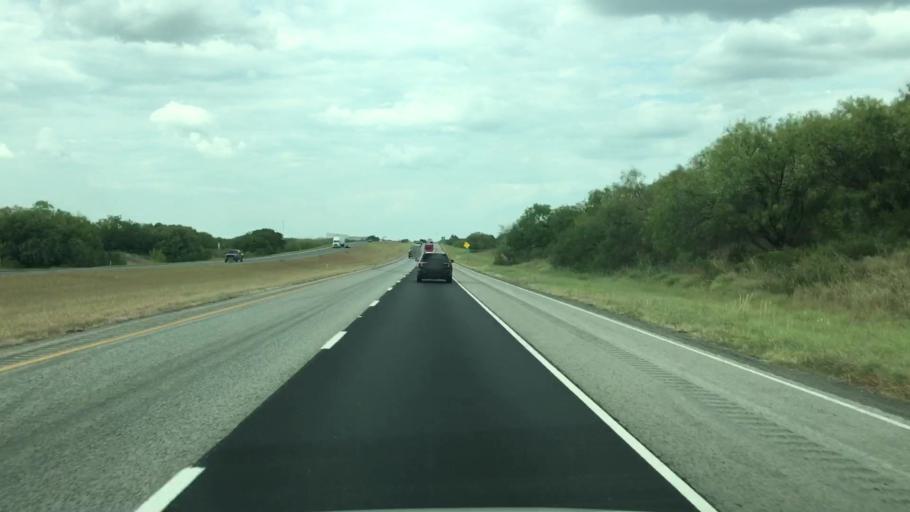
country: US
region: Texas
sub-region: Atascosa County
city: Pleasanton
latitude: 29.0818
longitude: -98.4328
